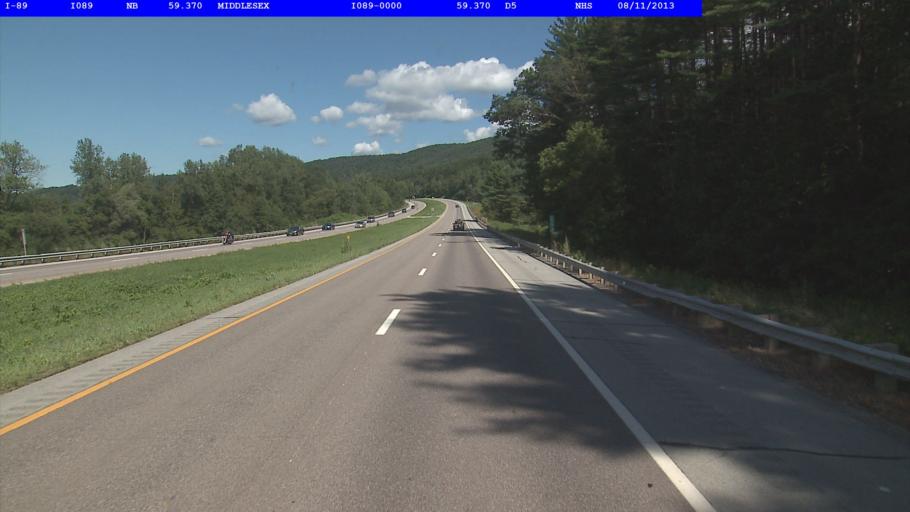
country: US
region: Vermont
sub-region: Washington County
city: Waterbury
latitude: 44.3065
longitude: -72.6911
